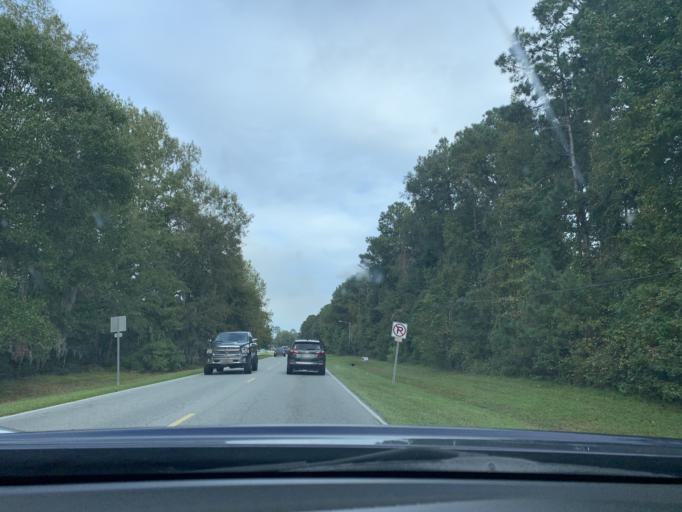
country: US
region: Georgia
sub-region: Chatham County
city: Pooler
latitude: 32.0938
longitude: -81.2630
